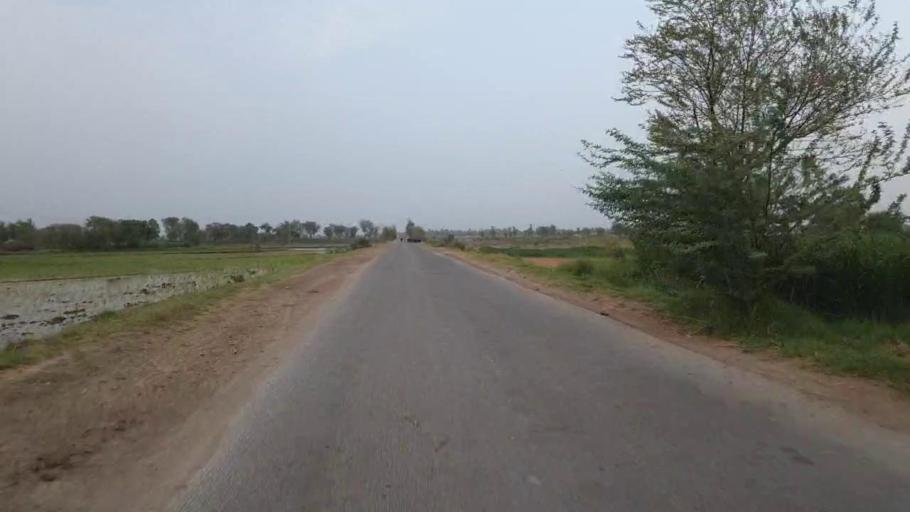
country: PK
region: Sindh
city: Daur
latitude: 26.4273
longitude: 68.2601
